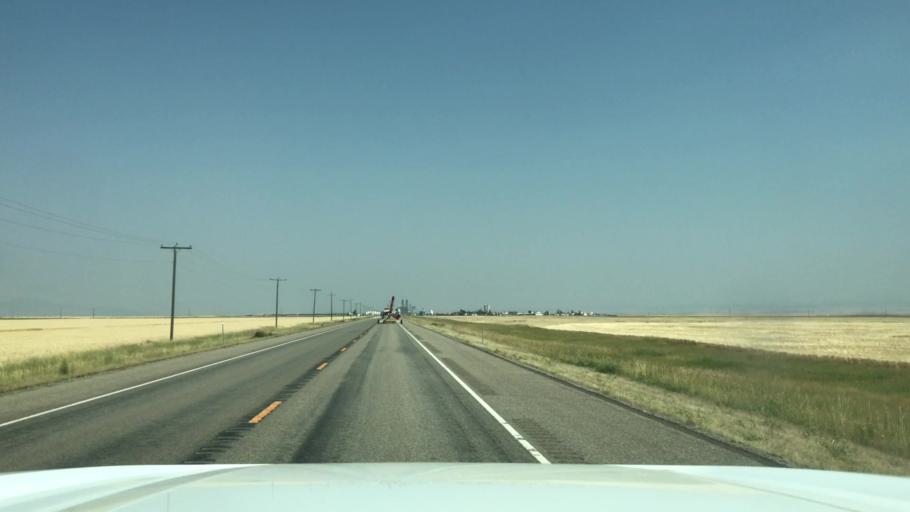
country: US
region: Montana
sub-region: Judith Basin County
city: Stanford
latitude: 47.0552
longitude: -109.9380
